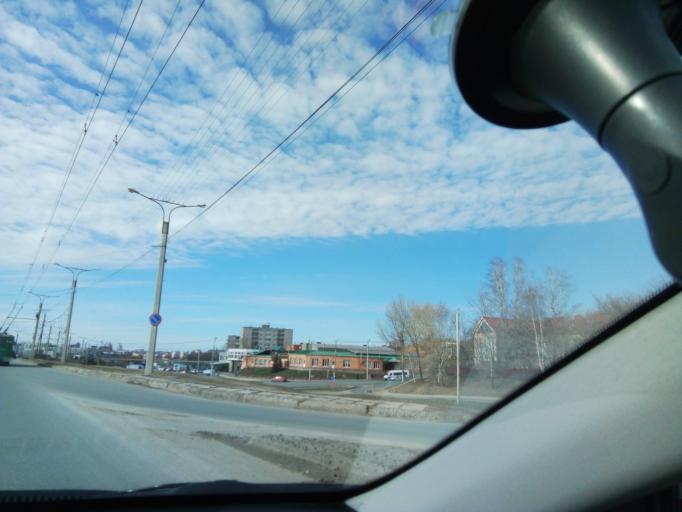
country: RU
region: Chuvashia
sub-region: Cheboksarskiy Rayon
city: Cheboksary
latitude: 56.1210
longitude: 47.2485
